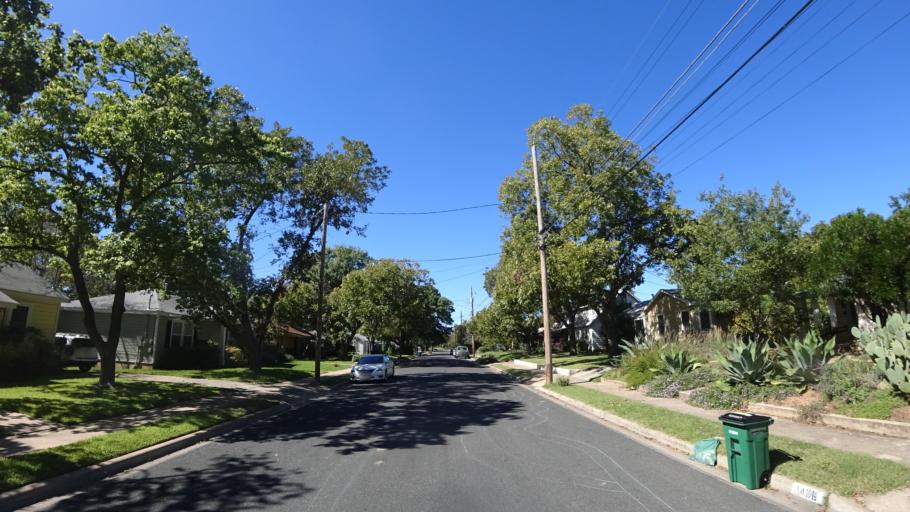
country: US
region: Texas
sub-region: Travis County
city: Austin
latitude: 30.3369
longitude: -97.7296
